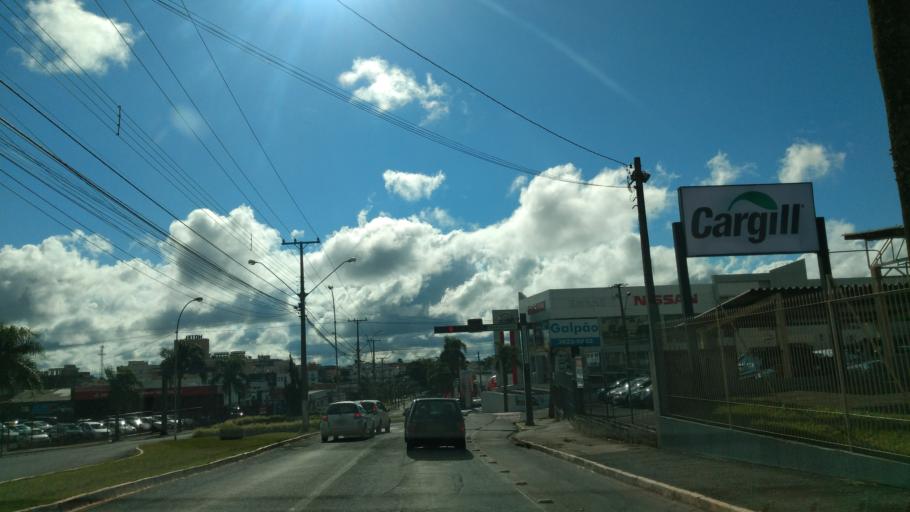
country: BR
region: Parana
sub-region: Guarapuava
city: Guarapuava
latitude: -25.3800
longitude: -51.4709
